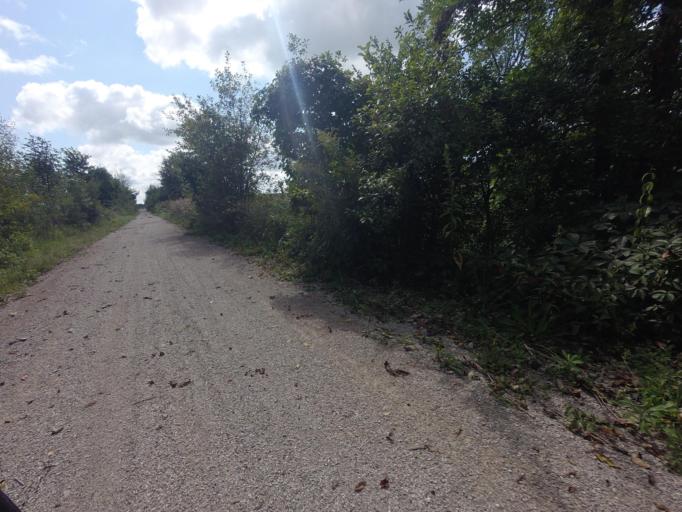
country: CA
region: Ontario
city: Huron East
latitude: 43.6539
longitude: -81.2355
